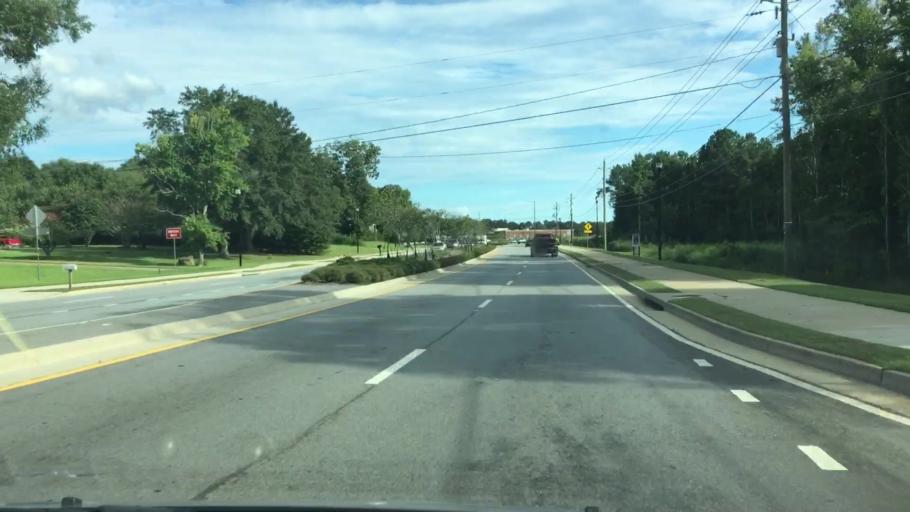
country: US
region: Georgia
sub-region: Clayton County
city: Conley
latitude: 33.6233
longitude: -84.2546
